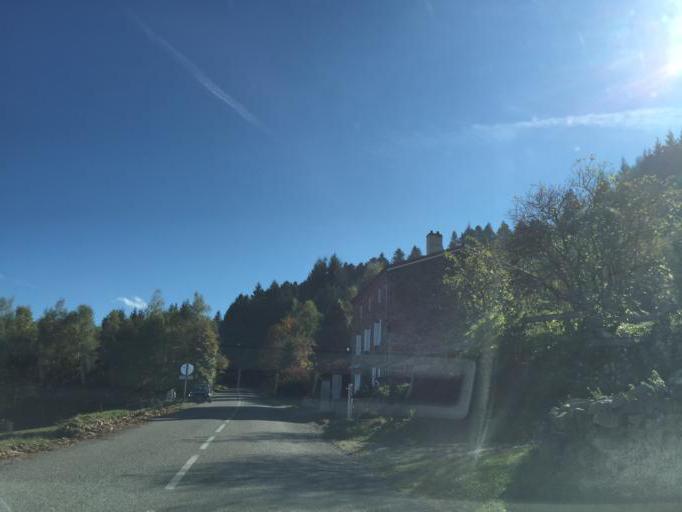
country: FR
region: Rhone-Alpes
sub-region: Departement de la Loire
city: Saint-Chamond
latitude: 45.3965
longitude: 4.5341
